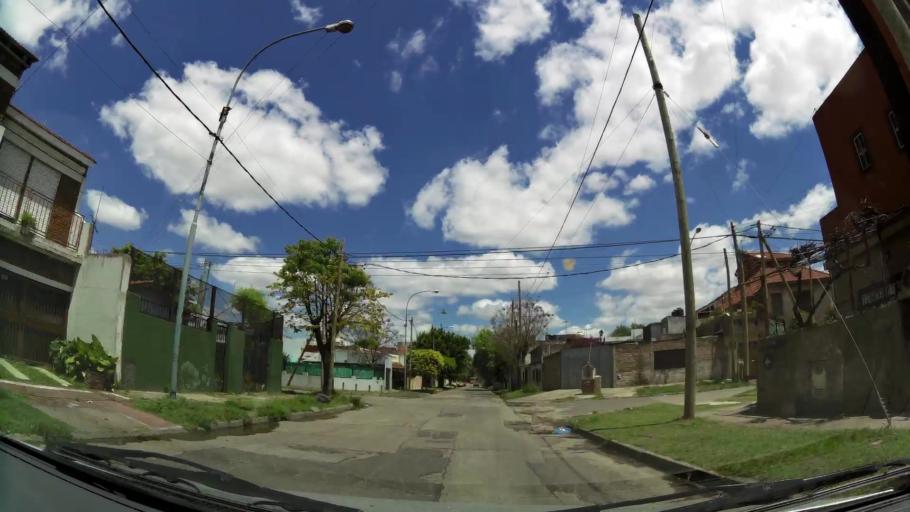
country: AR
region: Buenos Aires
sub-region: Partido de Lanus
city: Lanus
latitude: -34.7145
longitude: -58.4118
